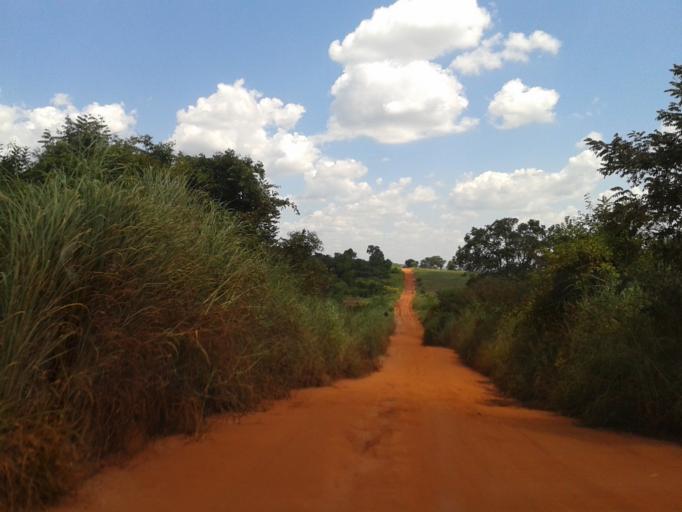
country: BR
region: Minas Gerais
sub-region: Ituiutaba
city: Ituiutaba
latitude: -19.0169
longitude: -49.6846
